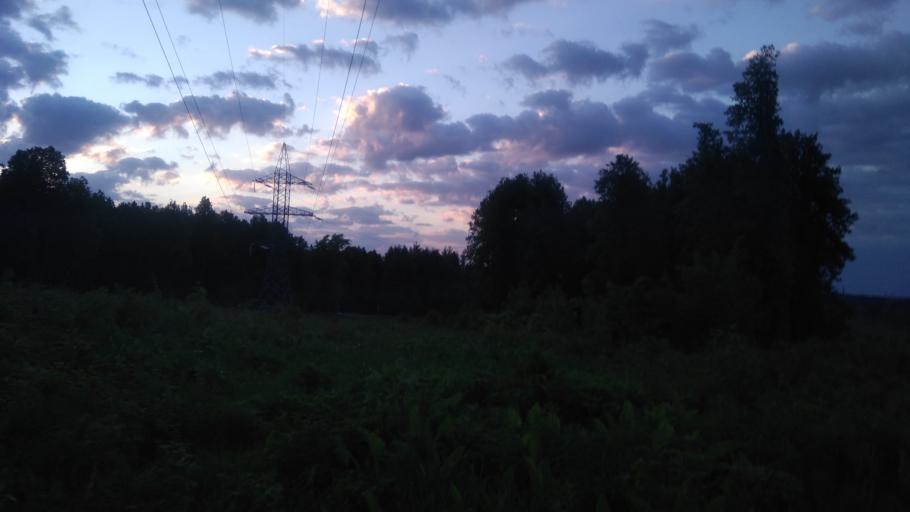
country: RU
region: Perm
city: Ferma
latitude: 57.9717
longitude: 56.3437
